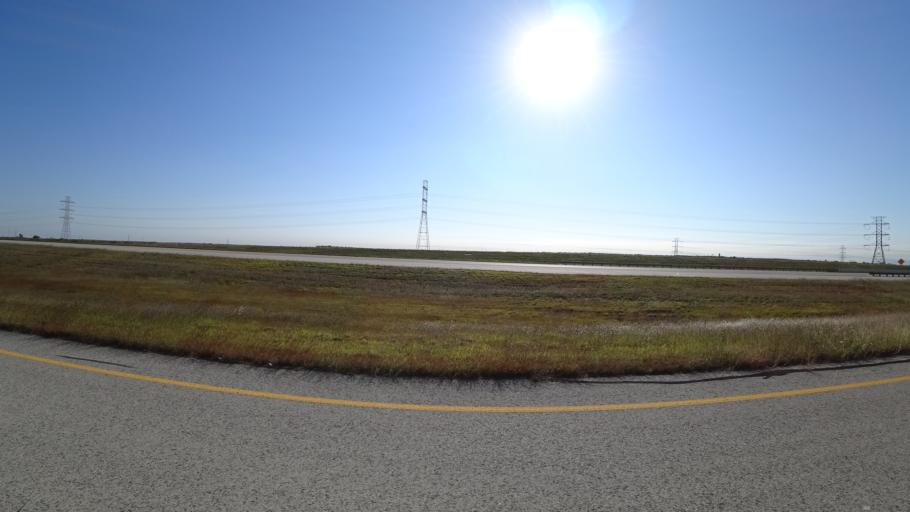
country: US
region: Texas
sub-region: Travis County
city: Onion Creek
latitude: 30.0876
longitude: -97.6854
